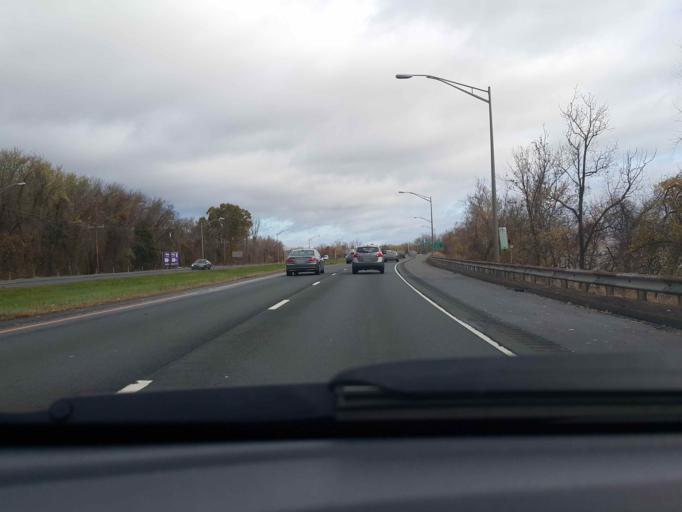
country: US
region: Connecticut
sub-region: Middlesex County
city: Portland
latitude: 41.5773
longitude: -72.6510
